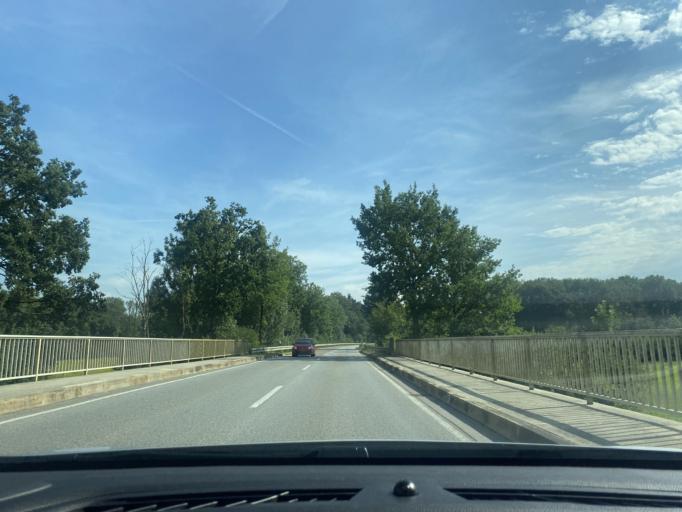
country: DE
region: Bavaria
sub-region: Upper Bavaria
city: Langenbach
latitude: 48.4563
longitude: 11.8525
